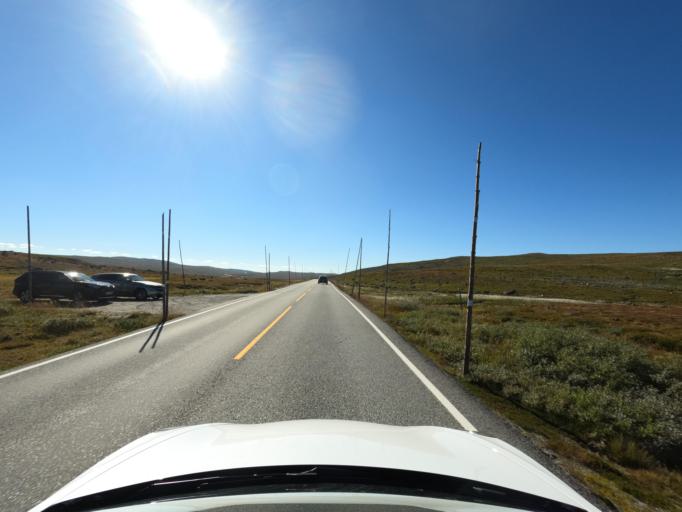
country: NO
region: Hordaland
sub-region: Eidfjord
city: Eidfjord
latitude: 60.4083
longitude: 7.6376
